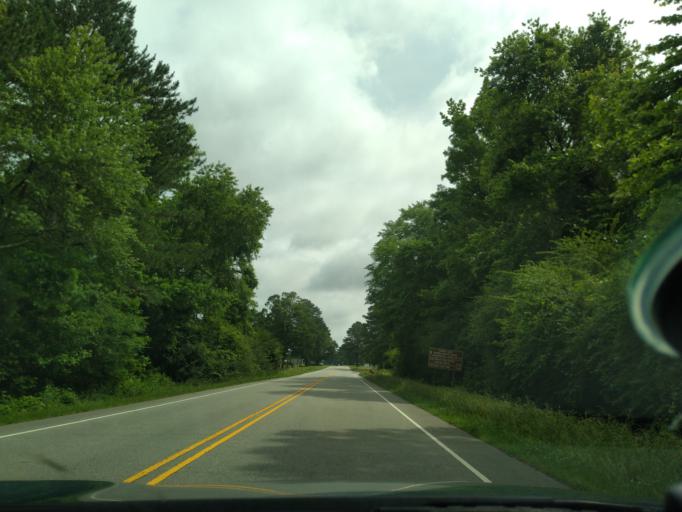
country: US
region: North Carolina
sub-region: Washington County
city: Plymouth
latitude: 35.8810
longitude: -76.6131
